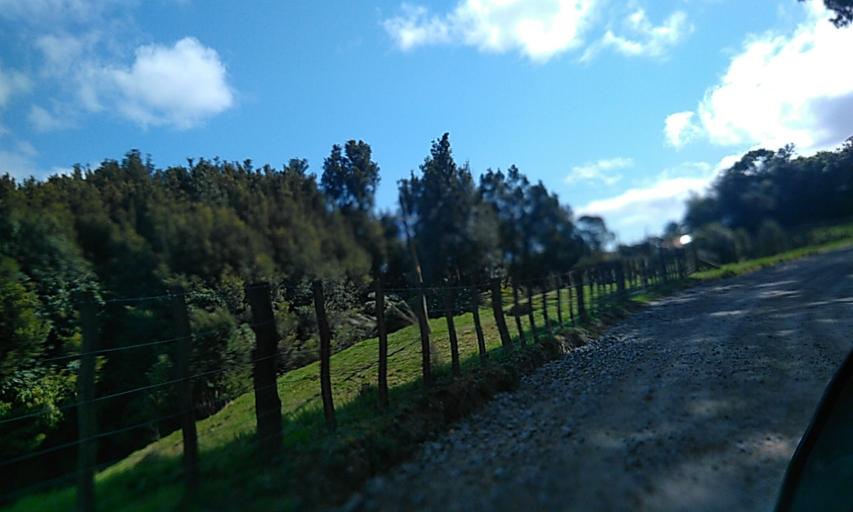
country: NZ
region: Gisborne
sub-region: Gisborne District
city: Gisborne
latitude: -38.2026
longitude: 178.0588
